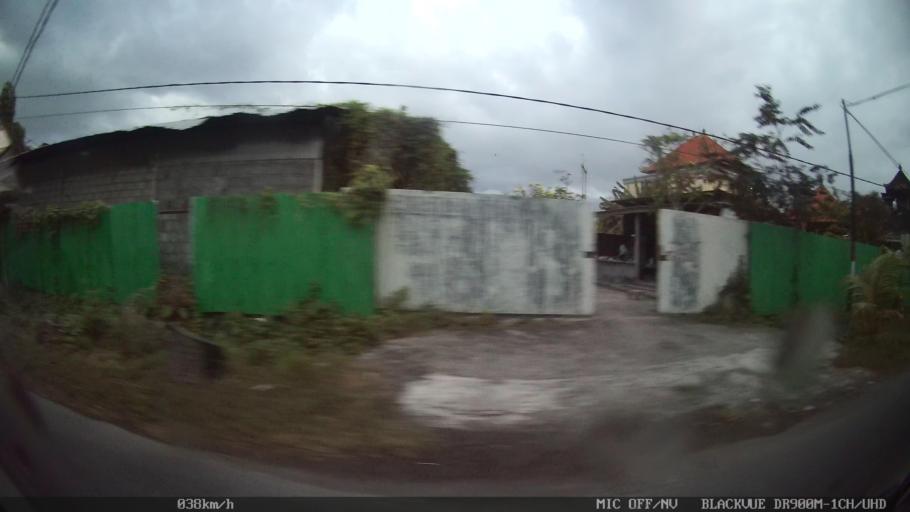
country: ID
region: Bali
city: Banjar Pasekan
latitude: -8.6402
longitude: 115.2819
